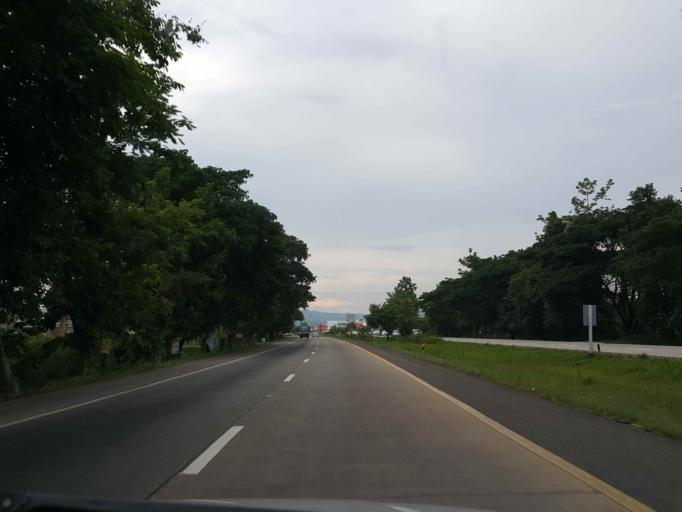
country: TH
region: Lampang
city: Hang Chat
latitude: 18.3210
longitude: 99.3387
